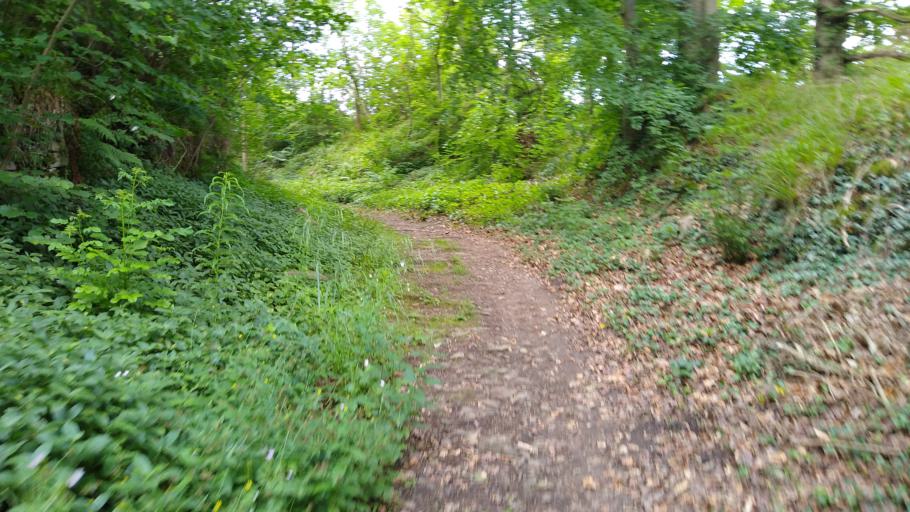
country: GB
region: England
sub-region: Northumberland
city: Haltwhistle
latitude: 54.9587
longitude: -2.4738
